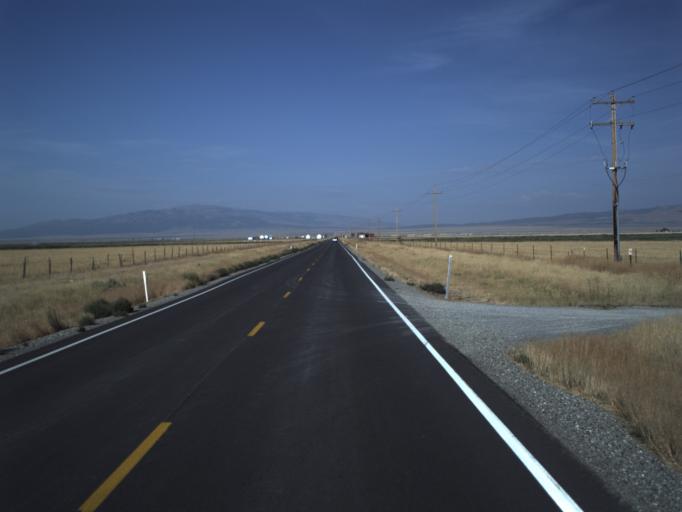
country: US
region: Idaho
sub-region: Oneida County
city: Malad City
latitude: 41.9672
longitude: -112.8528
